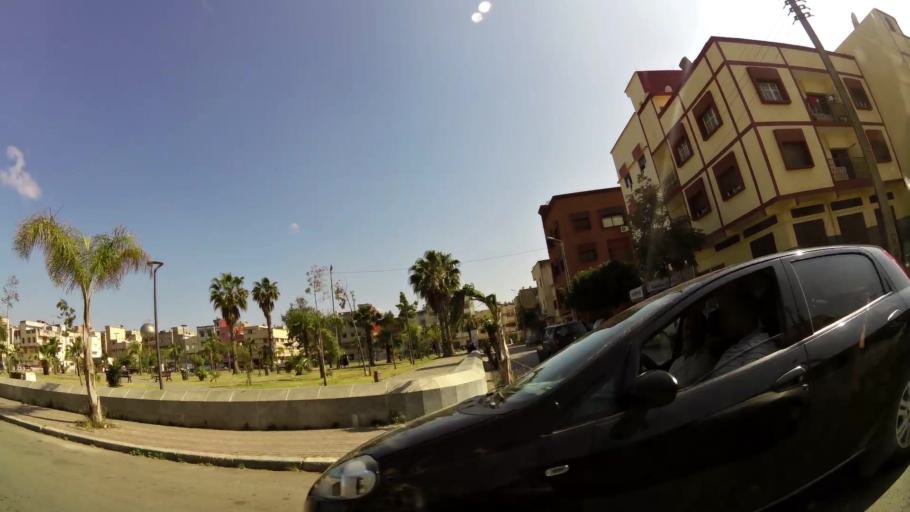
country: MA
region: Rabat-Sale-Zemmour-Zaer
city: Sale
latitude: 34.0429
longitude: -6.7829
